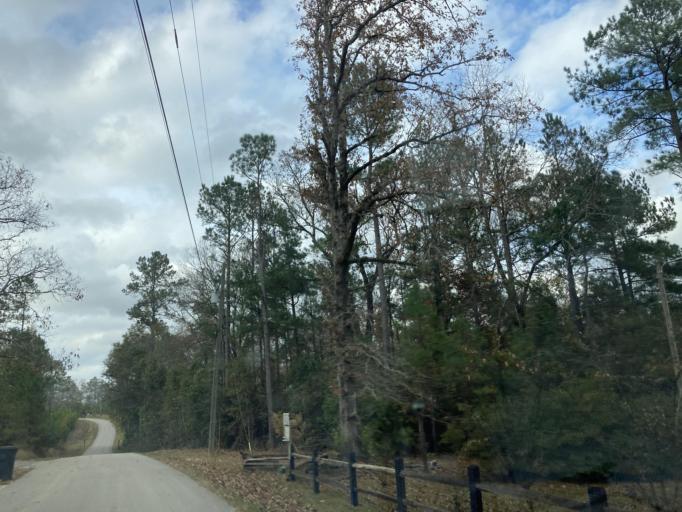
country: US
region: Mississippi
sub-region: Lamar County
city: Purvis
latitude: 31.1846
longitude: -89.5784
